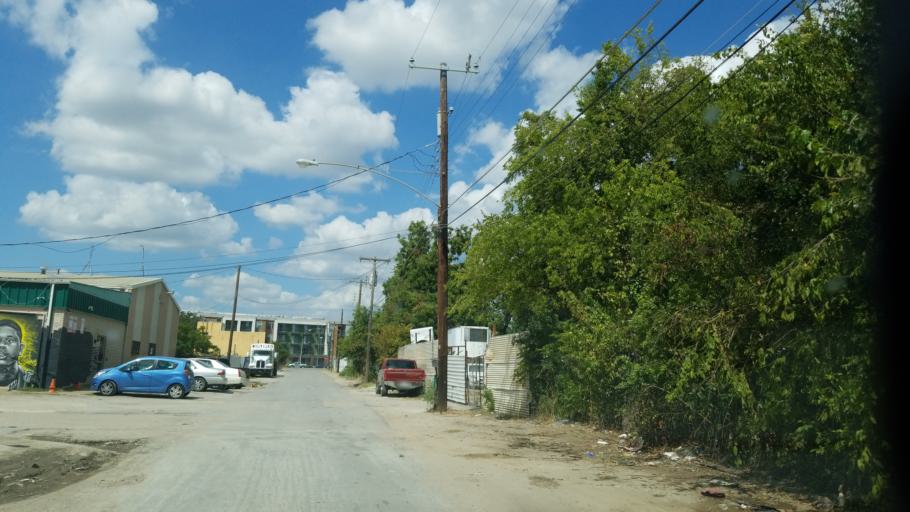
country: US
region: Texas
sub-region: Dallas County
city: Dallas
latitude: 32.7721
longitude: -96.8275
